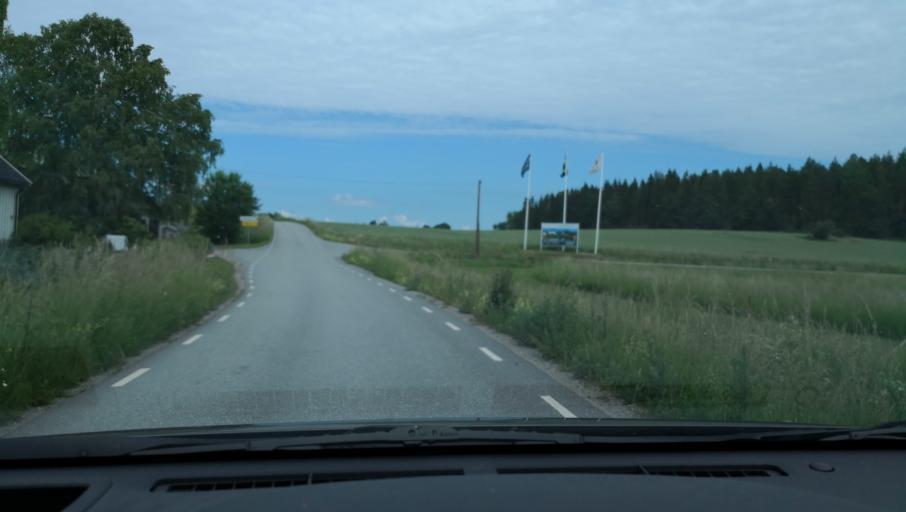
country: SE
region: Uppsala
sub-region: Habo Kommun
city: Balsta
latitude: 59.7041
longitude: 17.4757
